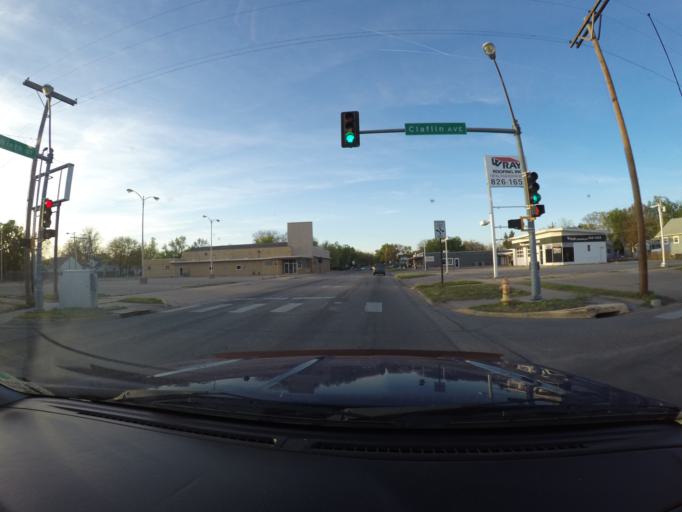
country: US
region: Kansas
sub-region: Saline County
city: Salina
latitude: 38.8145
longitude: -97.6128
